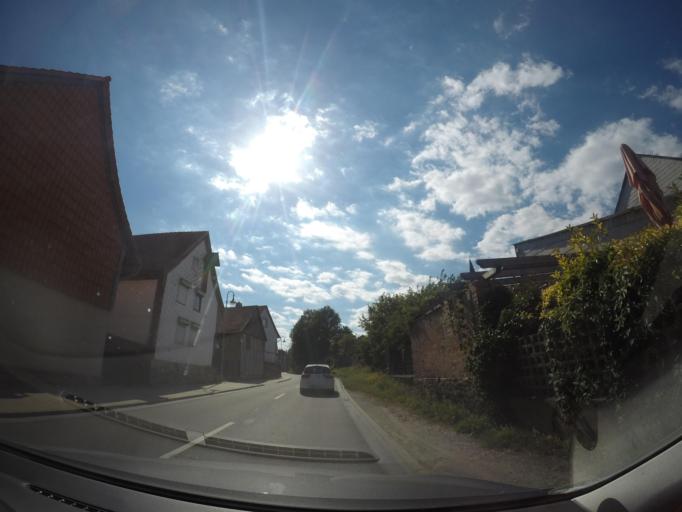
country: DE
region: Saxony-Anhalt
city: Langeln
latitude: 51.9112
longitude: 10.7944
